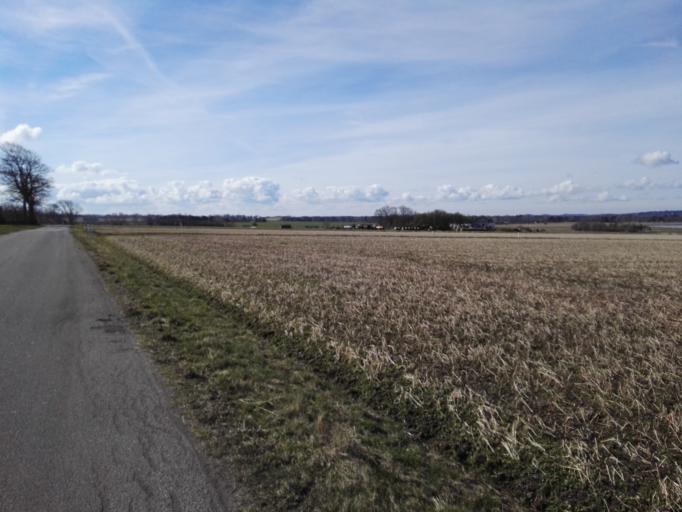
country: DK
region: Zealand
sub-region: Lejre Kommune
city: Ejby
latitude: 55.7857
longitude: 11.8338
